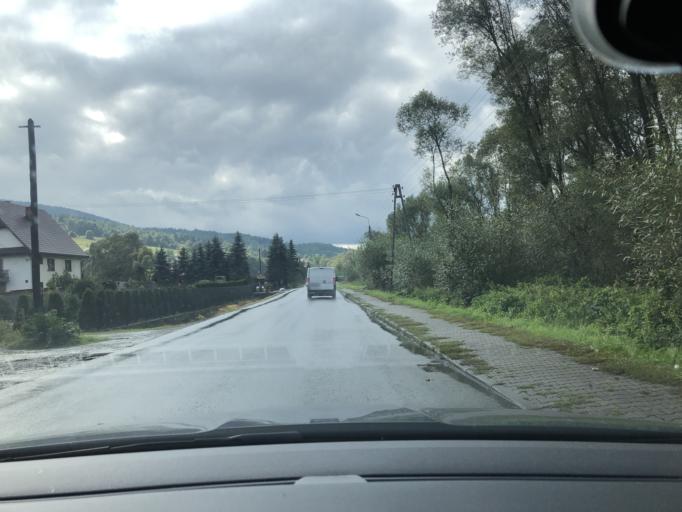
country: PL
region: Lesser Poland Voivodeship
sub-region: Powiat suski
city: Kukow
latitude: 49.7231
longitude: 19.5015
